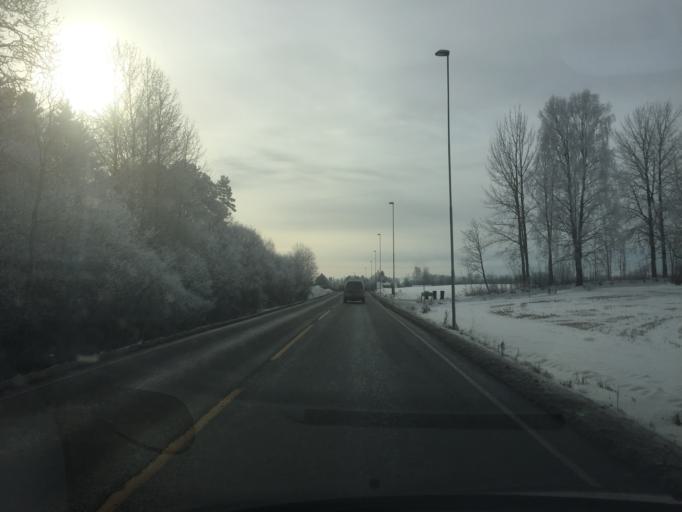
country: NO
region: Hedmark
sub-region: Loten
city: Loten
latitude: 60.8314
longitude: 11.3504
